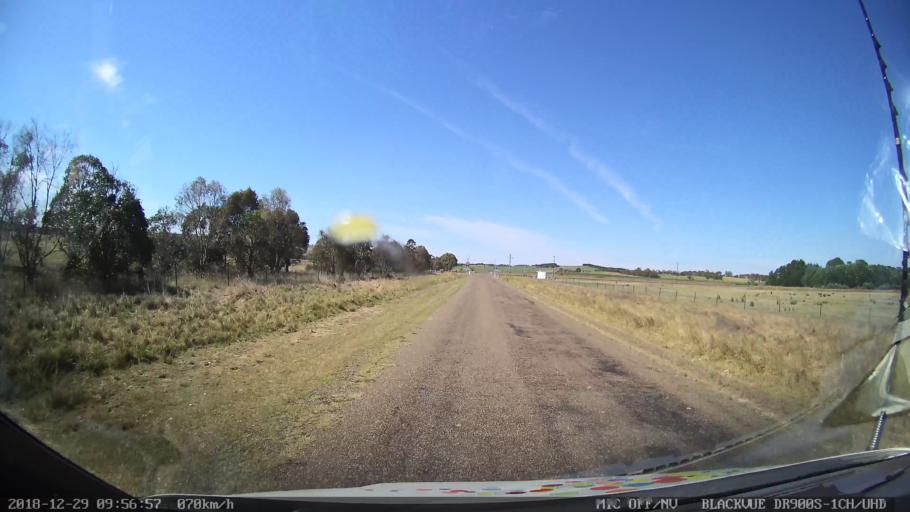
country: AU
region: New South Wales
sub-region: Goulburn Mulwaree
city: Goulburn
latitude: -34.7821
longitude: 149.4813
